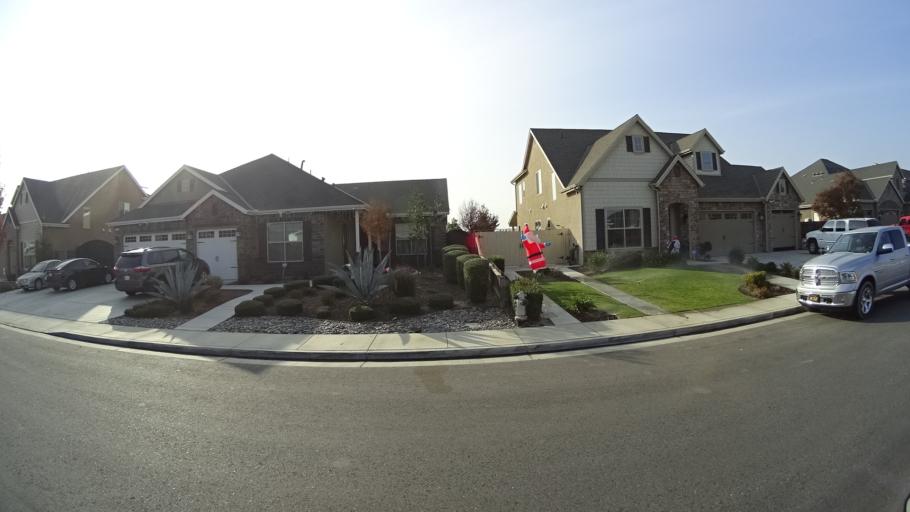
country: US
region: California
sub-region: Kern County
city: Greenacres
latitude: 35.4311
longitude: -119.1086
